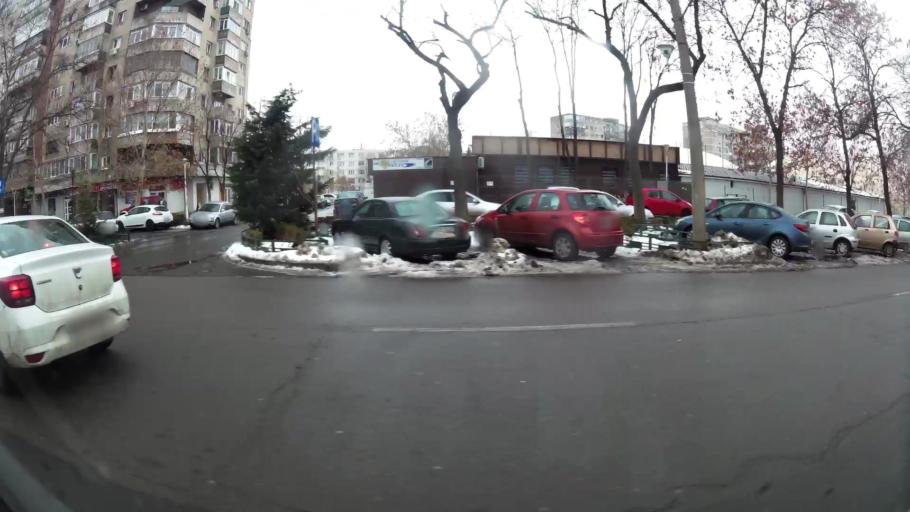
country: RO
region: Ilfov
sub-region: Comuna Chiajna
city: Rosu
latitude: 44.4182
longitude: 26.0323
